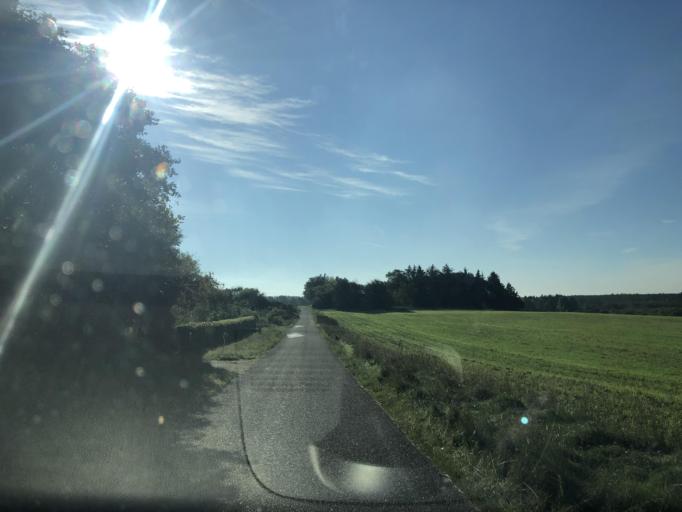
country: DK
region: Central Jutland
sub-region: Holstebro Kommune
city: Holstebro
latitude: 56.3107
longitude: 8.5043
